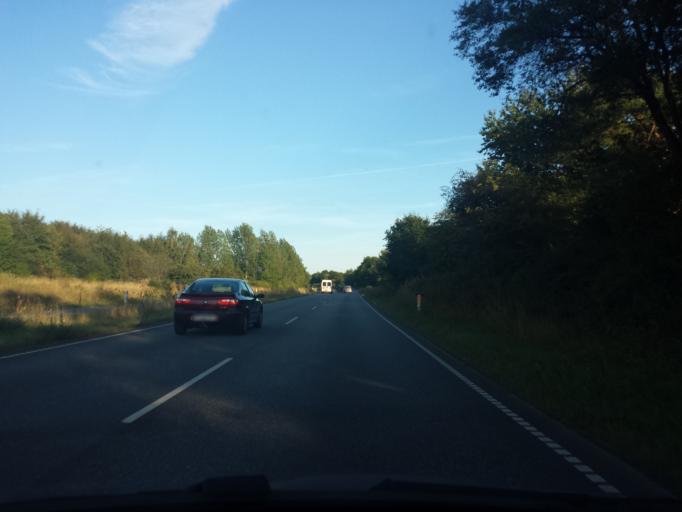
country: DK
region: Capital Region
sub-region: Egedal Kommune
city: Olstykke
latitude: 55.7814
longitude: 12.1645
